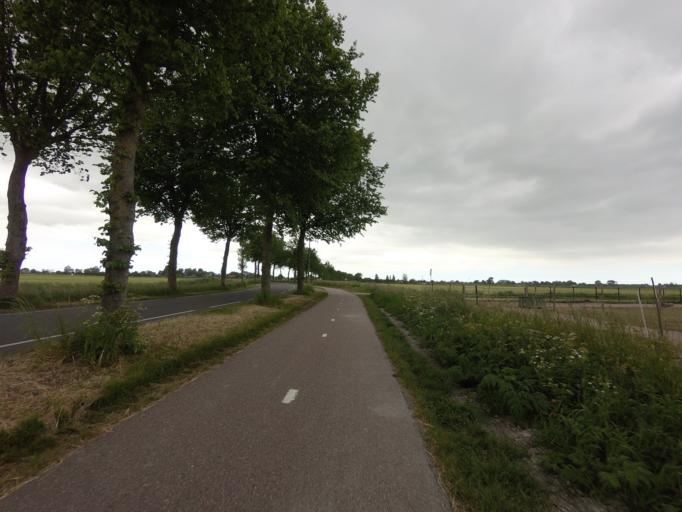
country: NL
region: North Holland
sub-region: Gemeente Hoorn
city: Hoorn
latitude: 52.6468
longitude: 5.0032
